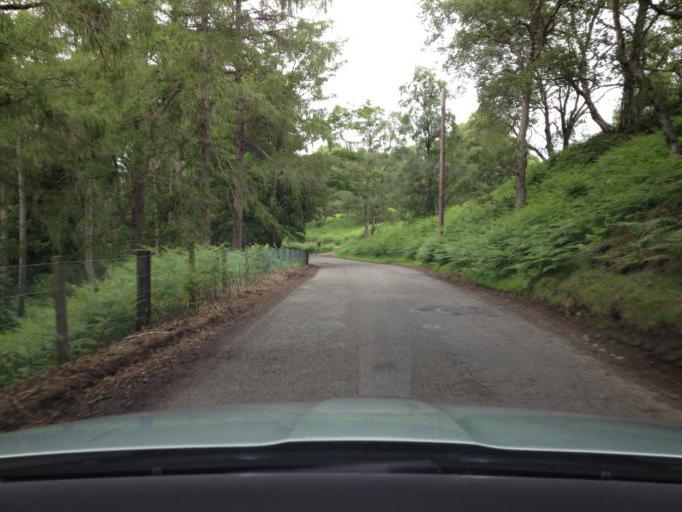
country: GB
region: Scotland
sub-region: Aberdeenshire
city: Aboyne
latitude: 56.8966
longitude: -2.7427
